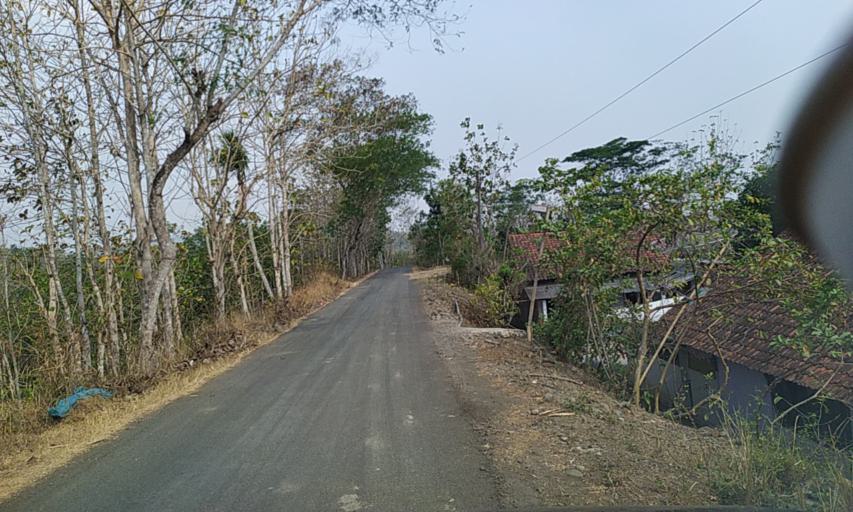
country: ID
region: Central Java
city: Karanggintung
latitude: -7.4657
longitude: 108.8836
